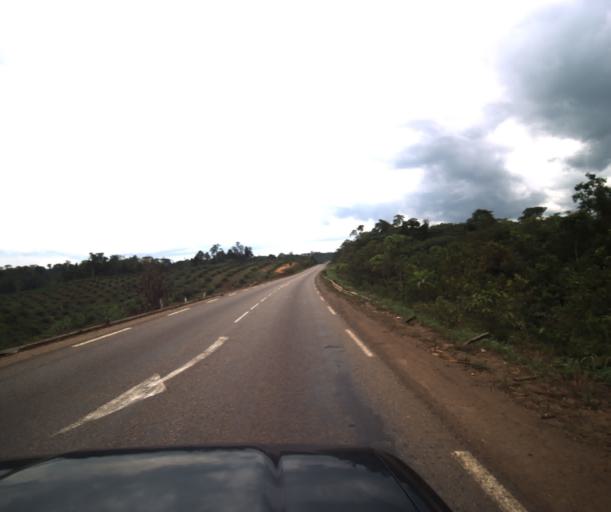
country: CM
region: Littoral
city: Edea
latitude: 3.8659
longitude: 10.0749
